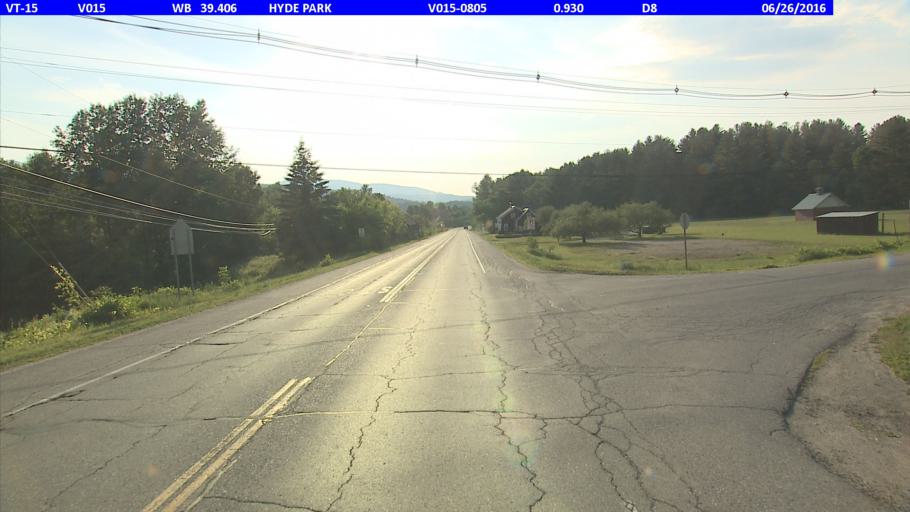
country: US
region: Vermont
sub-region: Lamoille County
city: Hyde Park
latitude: 44.6003
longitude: -72.6333
